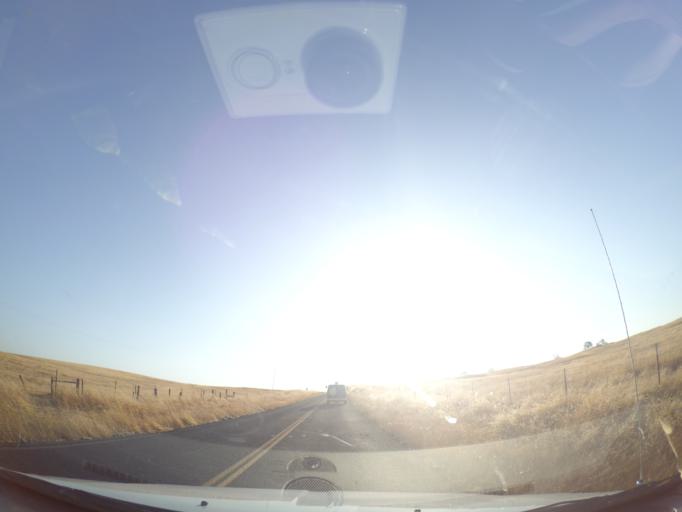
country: US
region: California
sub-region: Mariposa County
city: Mariposa
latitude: 37.4918
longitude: -120.1855
